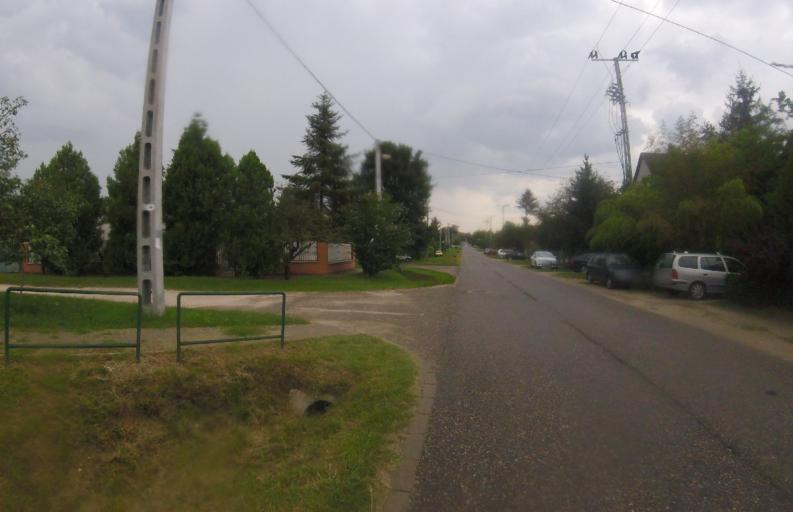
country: HU
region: Pest
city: God
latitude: 47.6749
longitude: 19.1398
